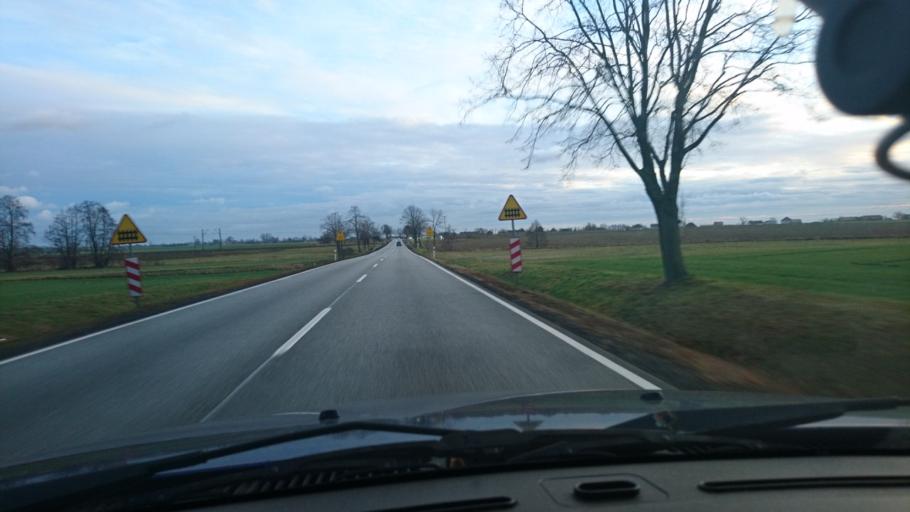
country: PL
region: Opole Voivodeship
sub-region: Powiat kluczborski
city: Kluczbork
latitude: 51.0185
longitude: 18.1977
